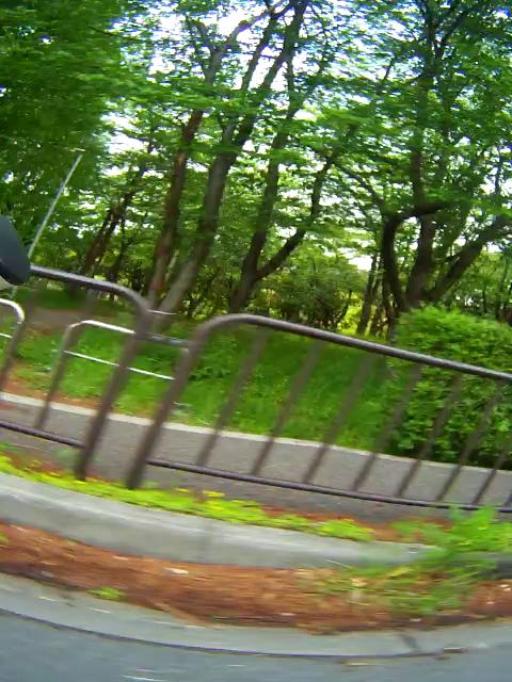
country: JP
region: Osaka
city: Toyonaka
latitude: 34.7776
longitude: 135.4924
